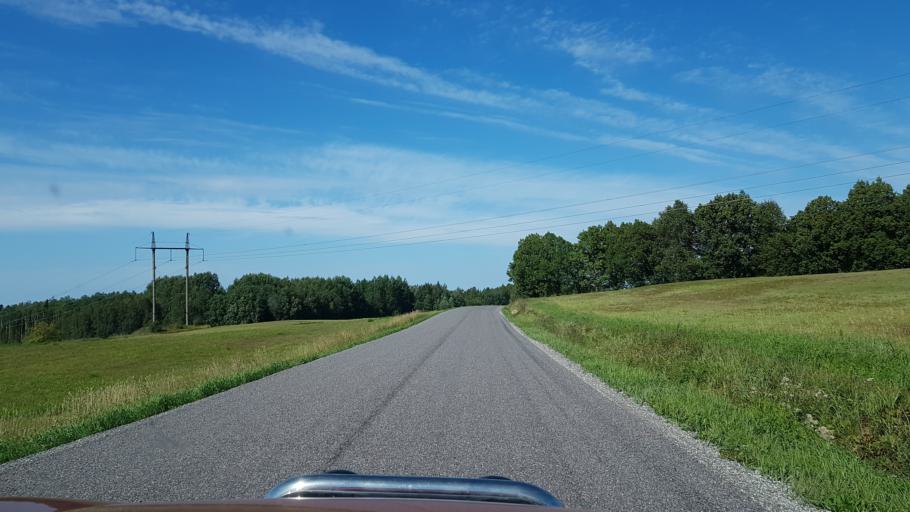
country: EE
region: Tartu
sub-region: Elva linn
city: Elva
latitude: 58.2449
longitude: 26.3878
